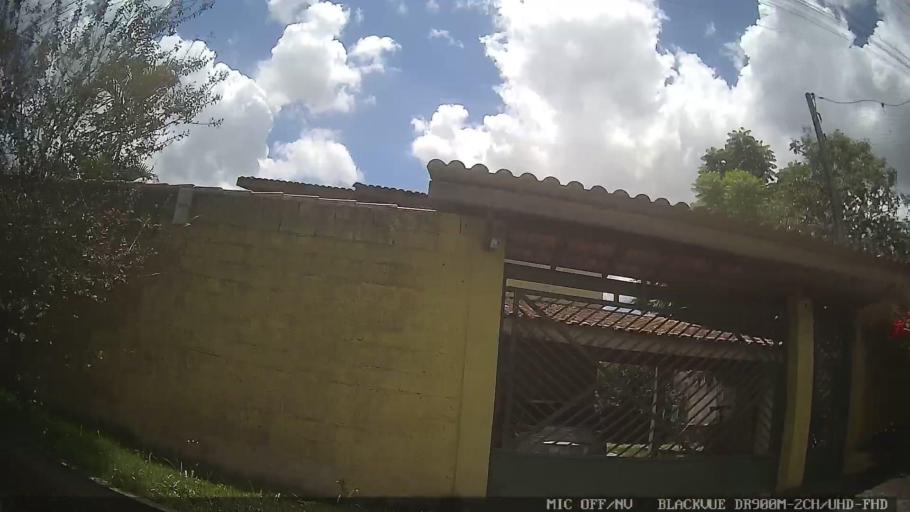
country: BR
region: Sao Paulo
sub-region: Atibaia
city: Atibaia
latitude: -23.1152
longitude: -46.5930
